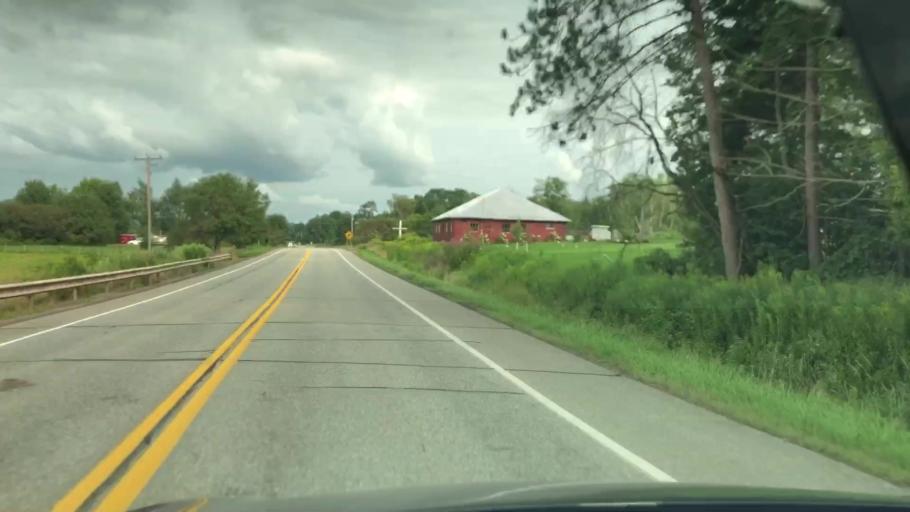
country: US
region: Pennsylvania
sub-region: Erie County
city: Northwest Harborcreek
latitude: 42.0598
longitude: -79.8678
